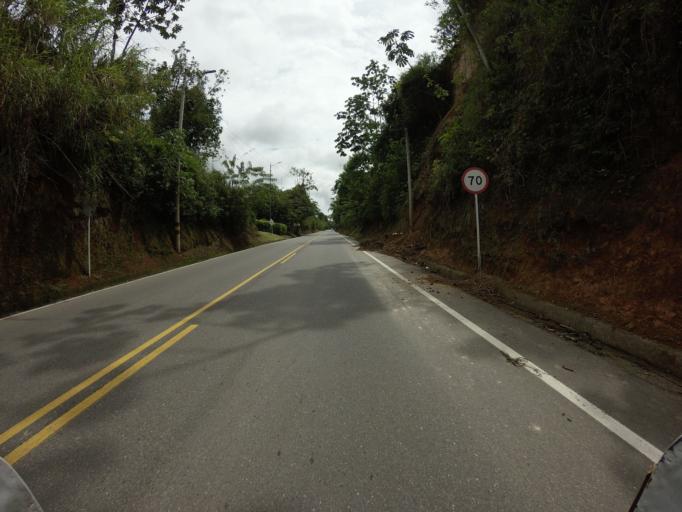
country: CO
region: Valle del Cauca
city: Alcala
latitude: 4.6534
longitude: -75.7759
